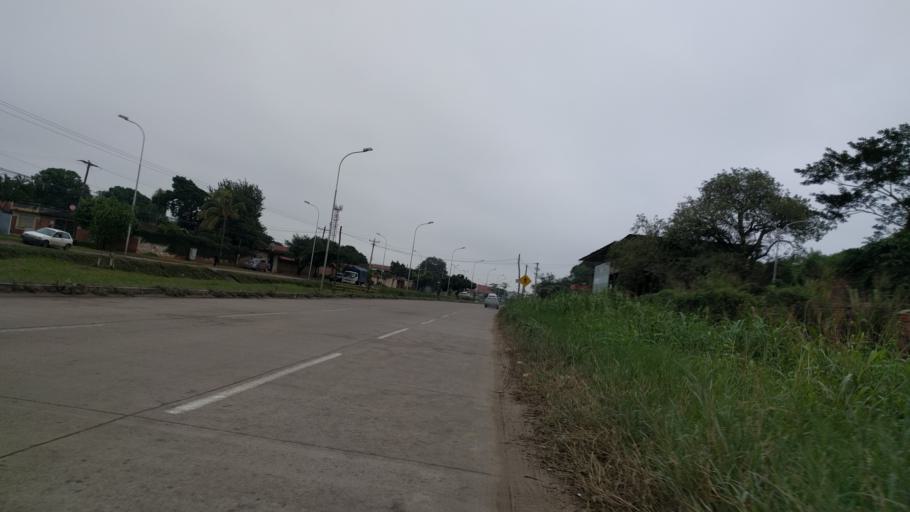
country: BO
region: Santa Cruz
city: Santa Cruz de la Sierra
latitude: -17.8326
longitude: -63.1920
